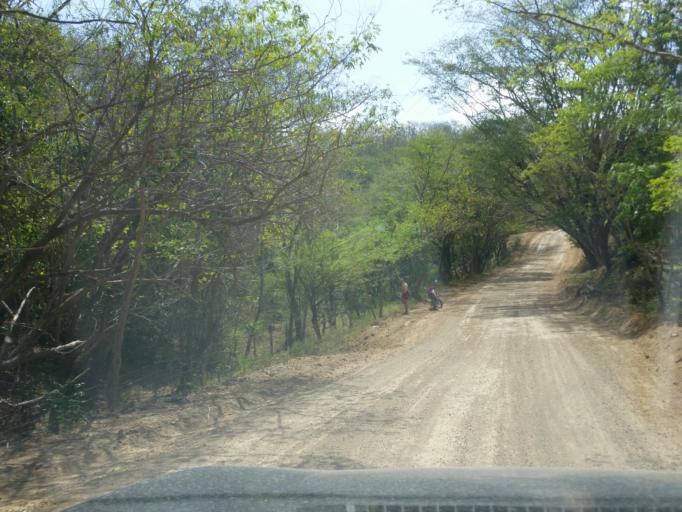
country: NI
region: Rivas
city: San Juan del Sur
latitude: 11.1473
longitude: -85.7909
